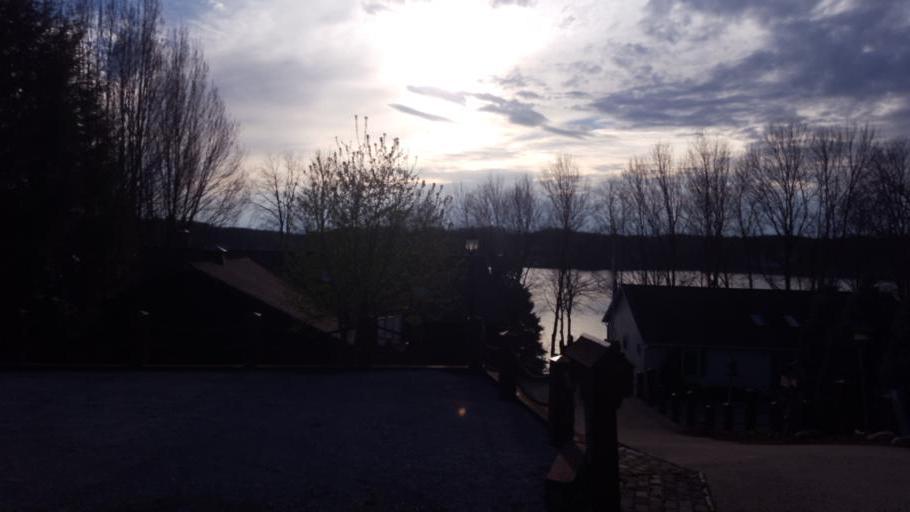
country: US
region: Ohio
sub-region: Knox County
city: Gambier
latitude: 40.4216
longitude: -82.3432
